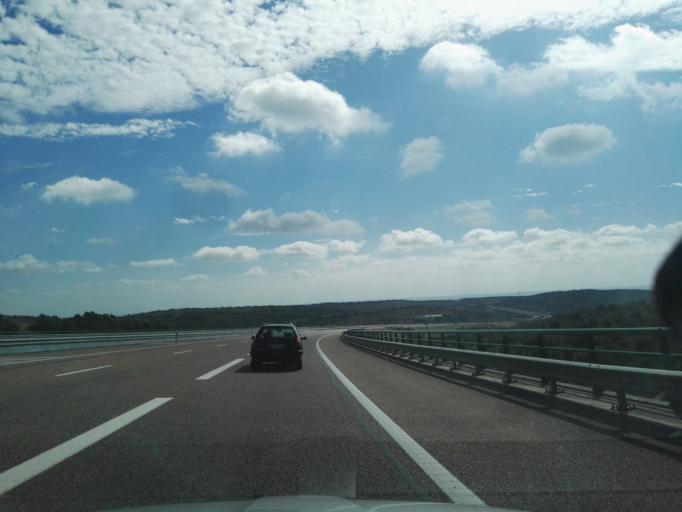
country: PT
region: Portalegre
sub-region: Elvas
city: Elvas
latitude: 38.9106
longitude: -7.1701
